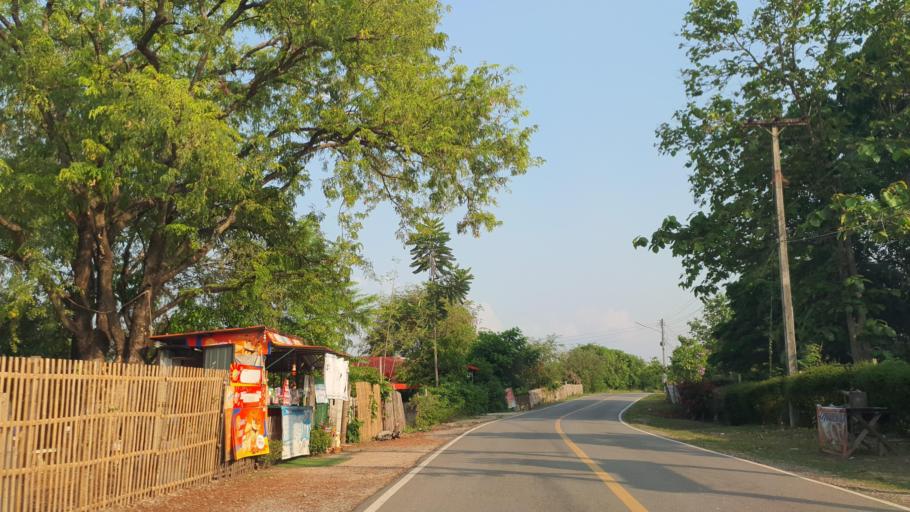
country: TH
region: Chiang Mai
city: Mae Wang
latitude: 18.6490
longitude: 98.8137
